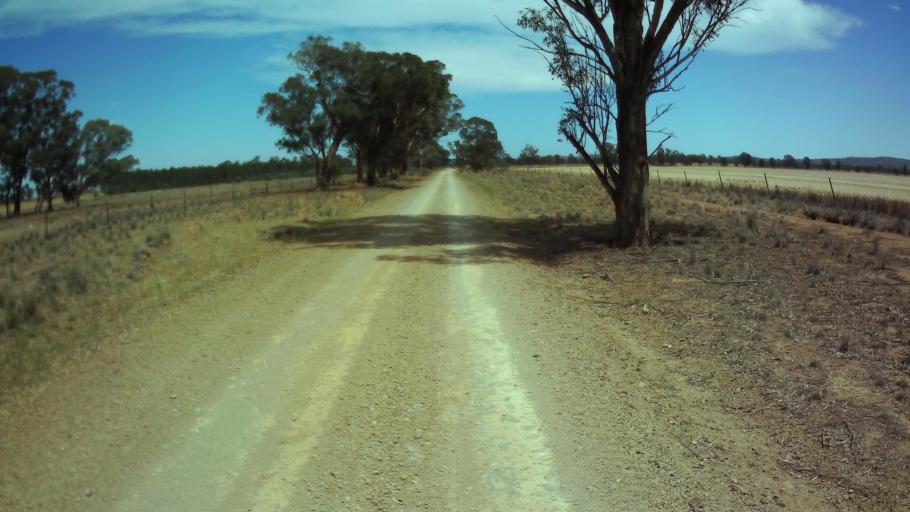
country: AU
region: New South Wales
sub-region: Weddin
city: Grenfell
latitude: -33.8570
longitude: 147.9115
